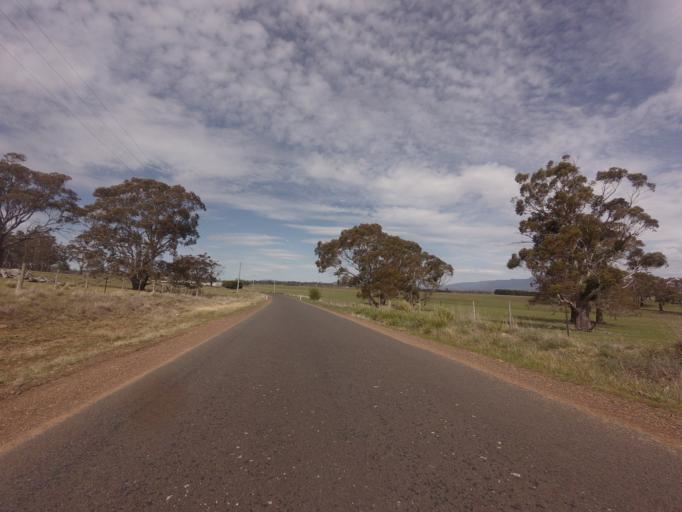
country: AU
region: Tasmania
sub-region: Northern Midlands
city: Longford
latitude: -41.7744
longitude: 147.2229
